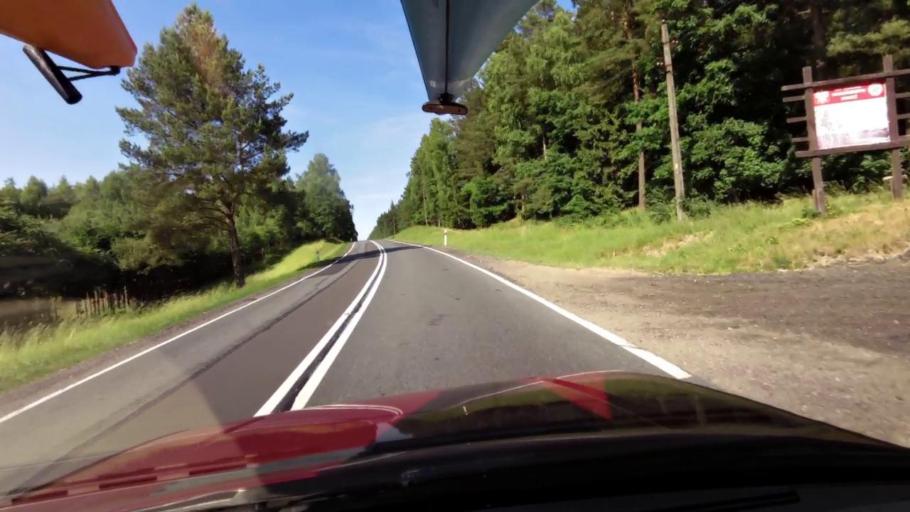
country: PL
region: Pomeranian Voivodeship
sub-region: Powiat bytowski
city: Miastko
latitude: 54.1142
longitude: 16.9989
